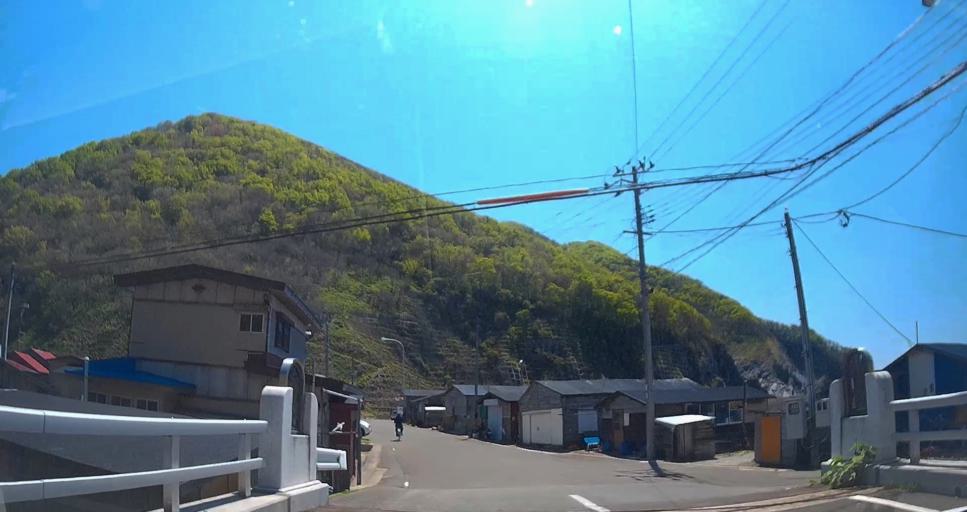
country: JP
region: Aomori
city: Mutsu
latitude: 41.3285
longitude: 140.8074
